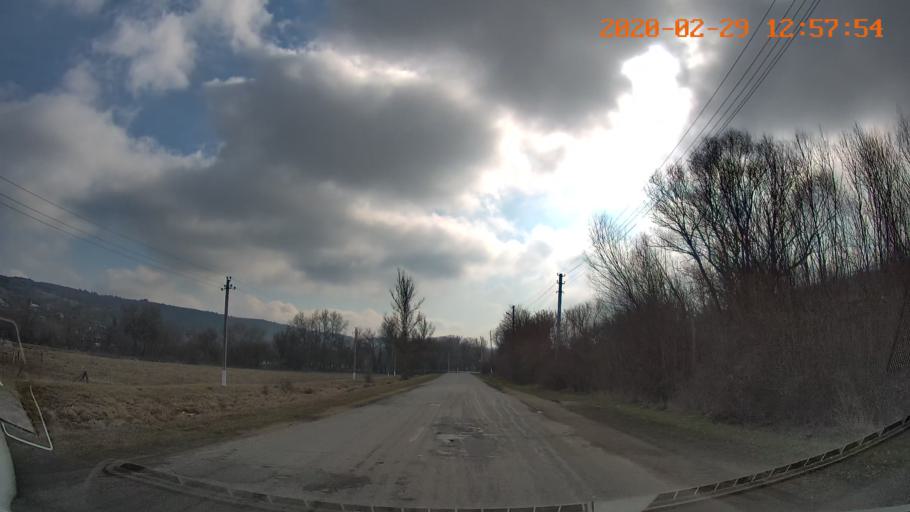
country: MD
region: Telenesti
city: Camenca
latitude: 48.0734
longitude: 28.7173
